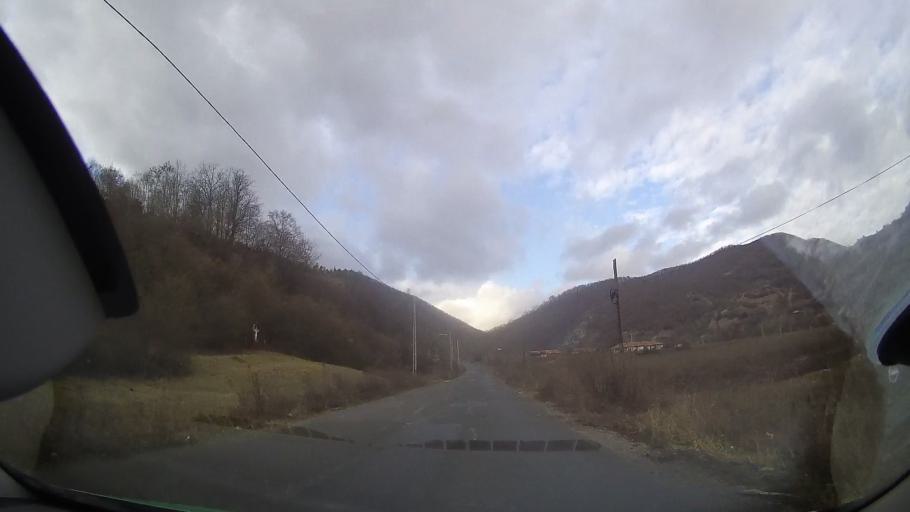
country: RO
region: Cluj
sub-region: Comuna Moldovenesti
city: Moldovenesti
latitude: 46.5035
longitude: 23.6040
